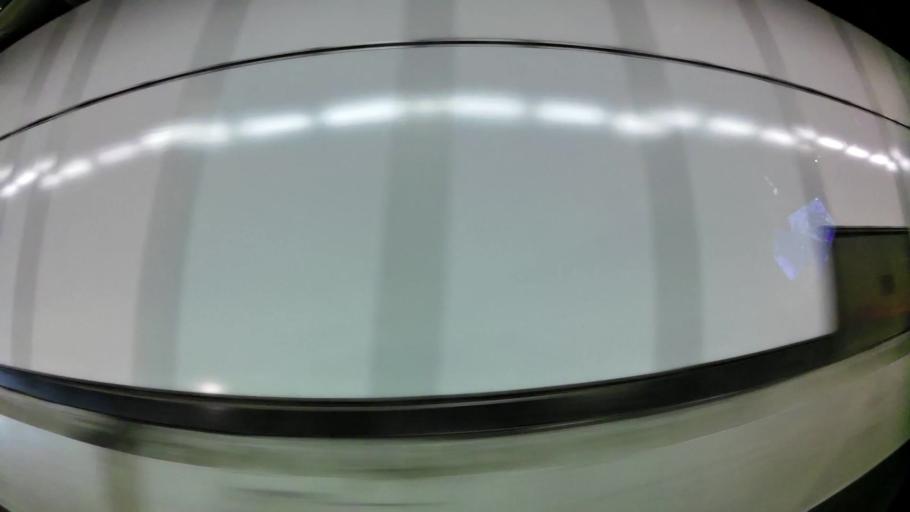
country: HK
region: Kowloon City
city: Kowloon
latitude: 22.2904
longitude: 114.2118
